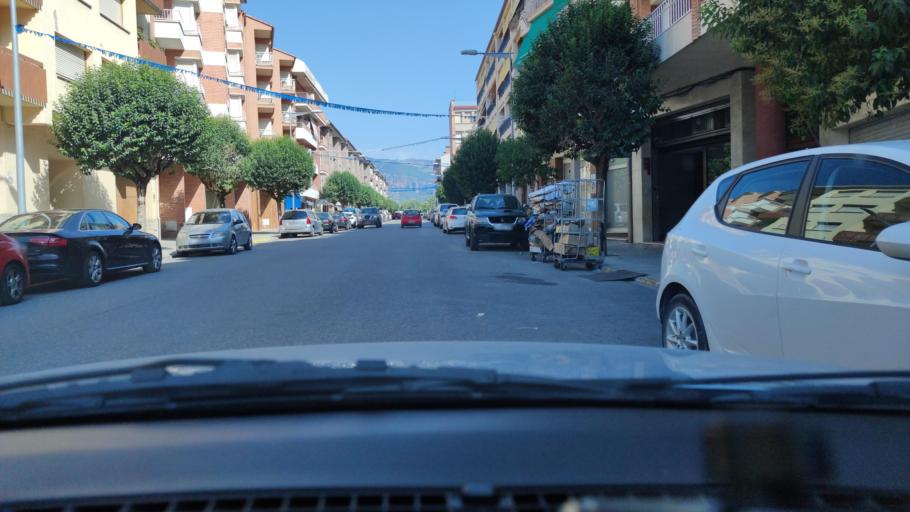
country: ES
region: Catalonia
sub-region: Provincia de Lleida
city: Senterada
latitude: 42.2493
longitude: 0.9658
